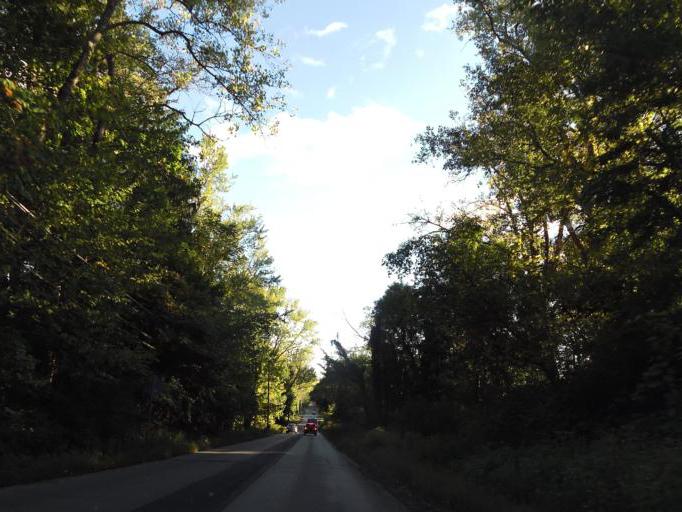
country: US
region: New York
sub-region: Erie County
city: Billington Heights
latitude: 42.7766
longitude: -78.6209
